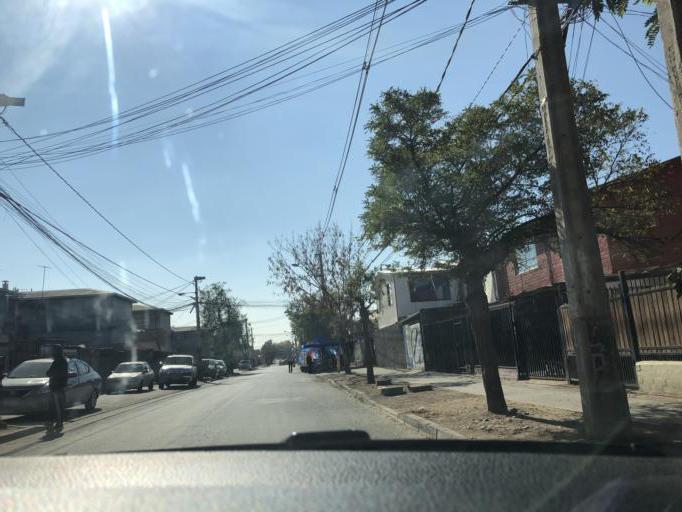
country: CL
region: Santiago Metropolitan
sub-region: Provincia de Santiago
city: La Pintana
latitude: -33.6245
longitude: -70.6242
